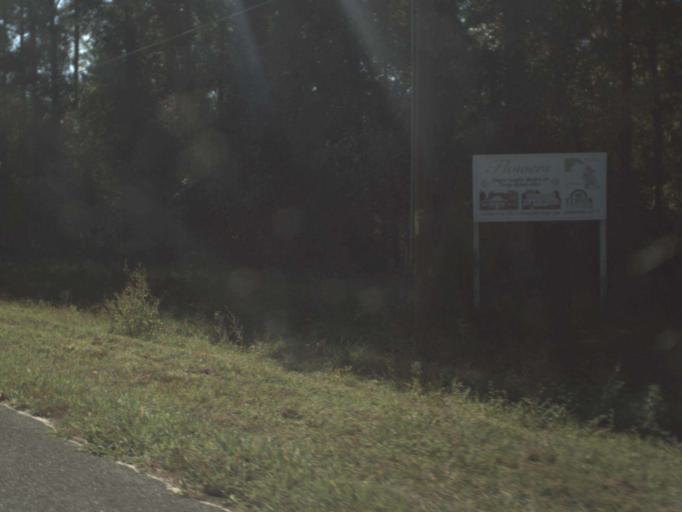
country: US
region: Florida
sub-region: Wakulla County
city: Crawfordville
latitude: 30.2688
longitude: -84.3709
